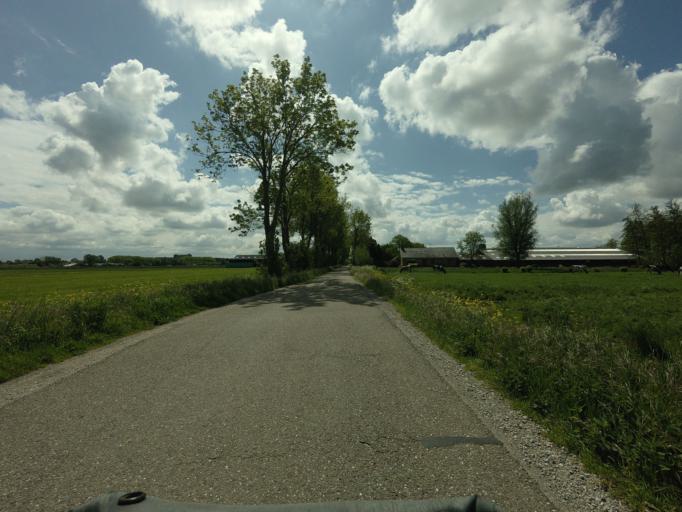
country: NL
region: South Holland
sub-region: Gemeente Gorinchem
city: Gorinchem
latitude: 51.8543
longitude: 4.9411
